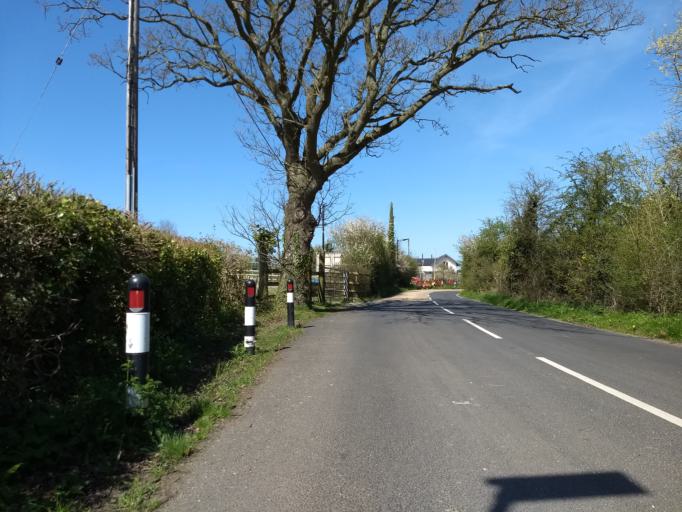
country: GB
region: England
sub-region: Isle of Wight
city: Gurnard
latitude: 50.7549
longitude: -1.3338
